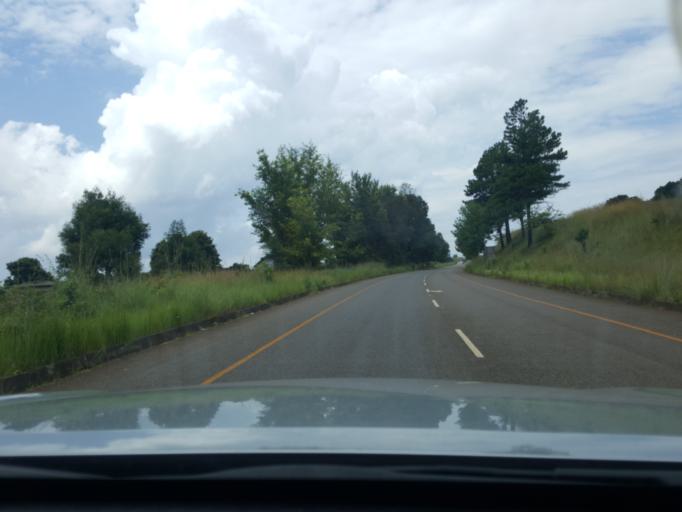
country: ZA
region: Mpumalanga
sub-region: Ehlanzeni District
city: Graksop
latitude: -25.1012
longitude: 30.7886
